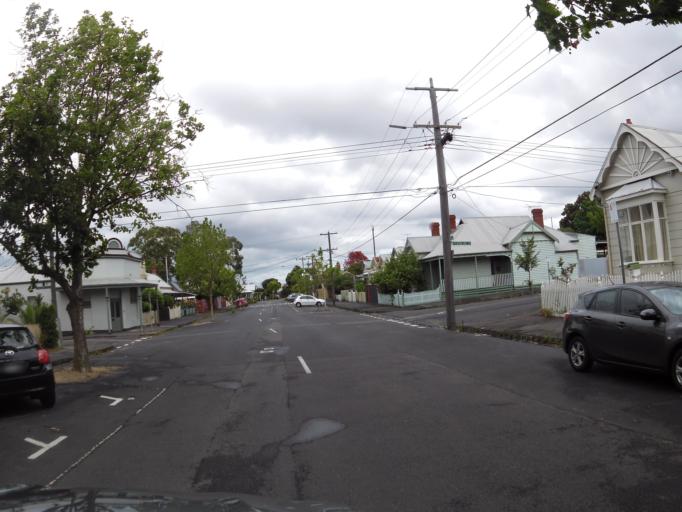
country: AU
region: Victoria
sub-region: Yarra
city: Clifton Hill
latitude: -37.7897
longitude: 145.0000
